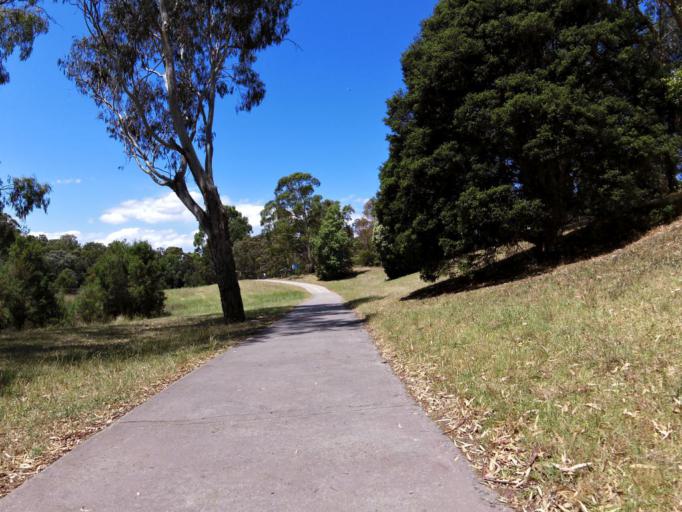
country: AU
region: Victoria
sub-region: Monash
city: Notting Hill
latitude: -37.8846
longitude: 145.1397
